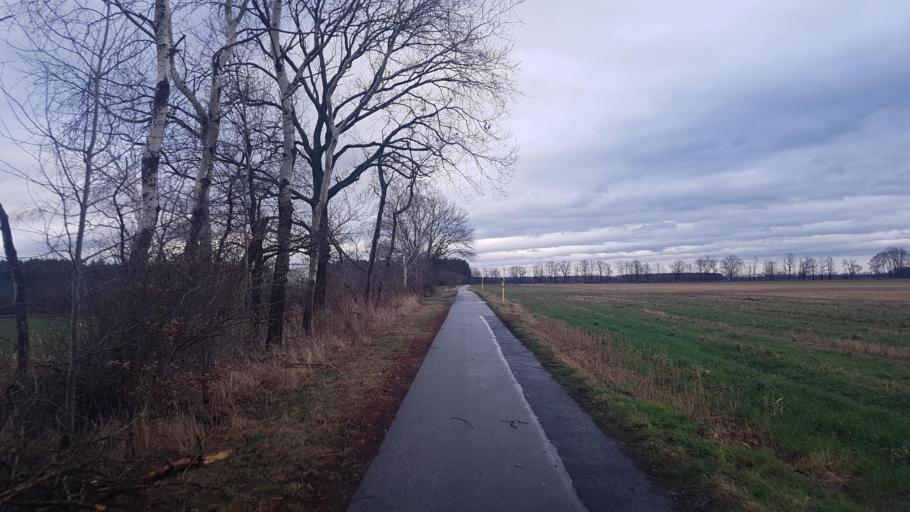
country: DE
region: Brandenburg
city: Plessa
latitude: 51.4355
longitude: 13.6413
